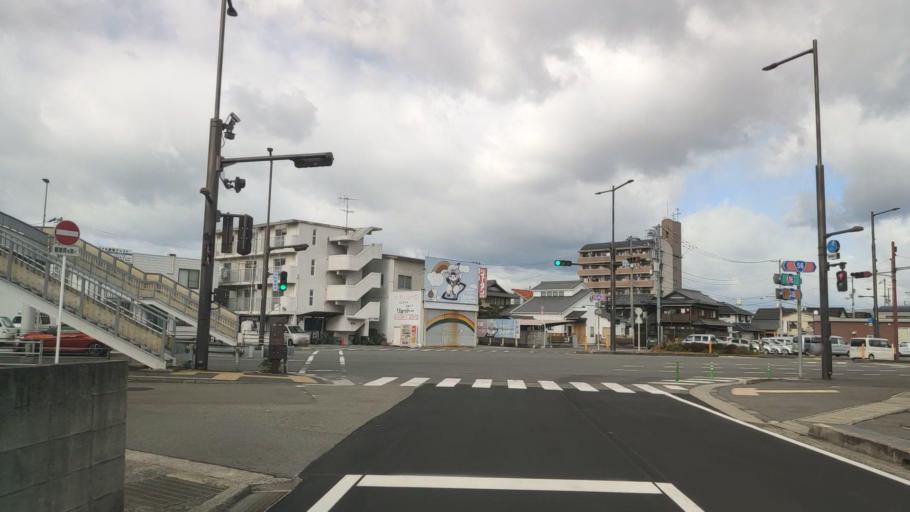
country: JP
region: Ehime
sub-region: Shikoku-chuo Shi
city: Matsuyama
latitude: 33.8231
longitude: 132.7575
